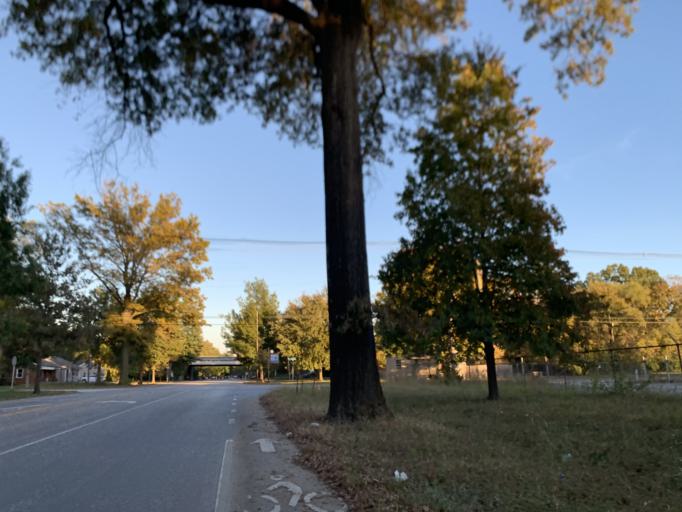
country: US
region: Kentucky
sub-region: Jefferson County
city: Shively
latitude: 38.2259
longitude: -85.8243
